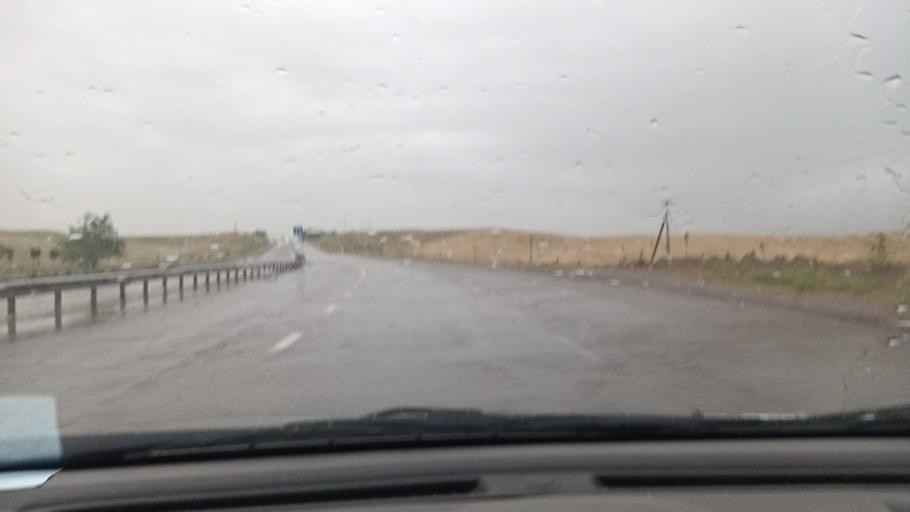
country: UZ
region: Toshkent
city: Ohangaron
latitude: 40.9690
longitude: 69.5486
